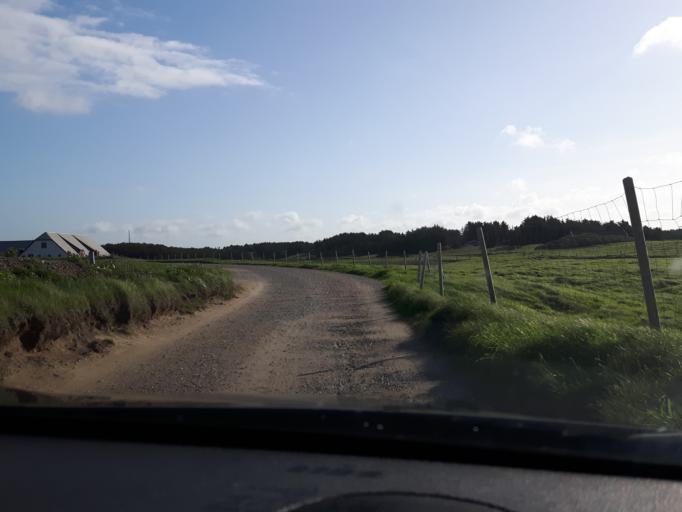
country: DK
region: North Denmark
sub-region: Hjorring Kommune
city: Hjorring
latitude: 57.4623
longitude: 9.7850
